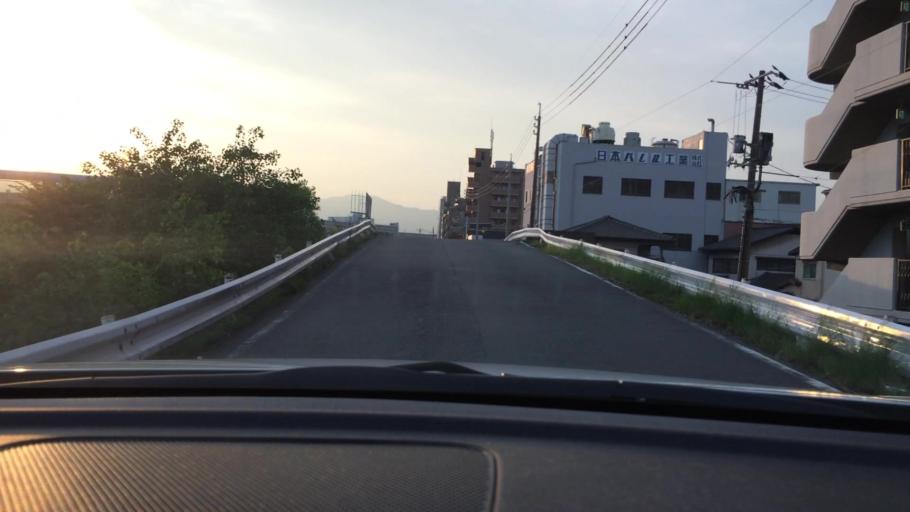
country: JP
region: Hiroshima
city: Hiroshima-shi
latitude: 34.3856
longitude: 132.4896
